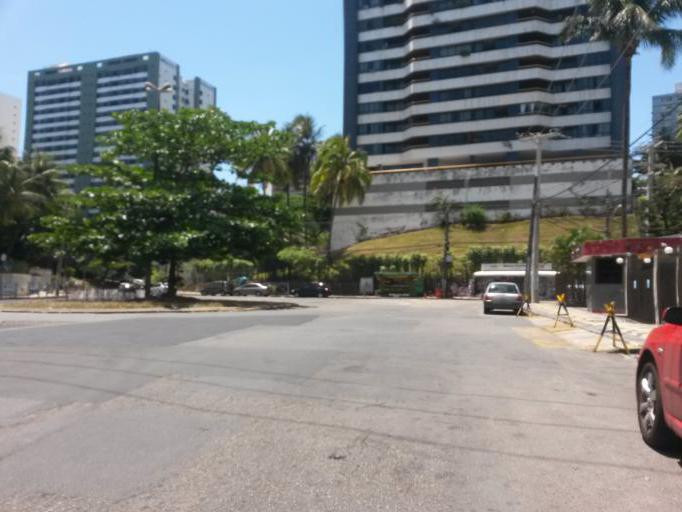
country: BR
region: Bahia
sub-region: Salvador
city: Salvador
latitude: -13.0043
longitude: -38.4609
